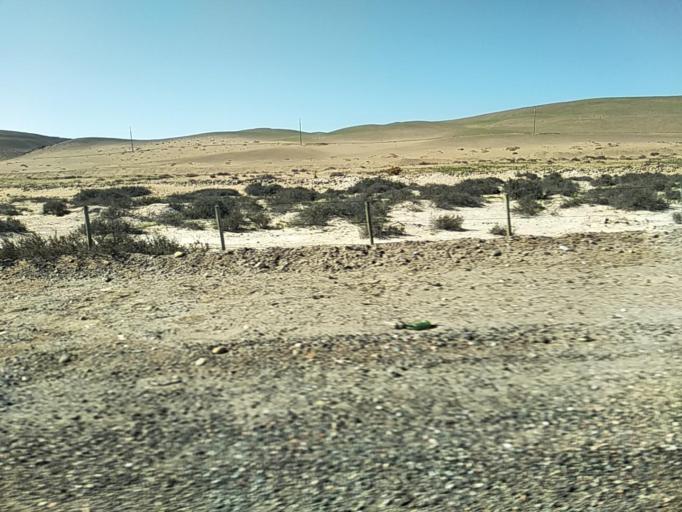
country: CL
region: Atacama
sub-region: Provincia de Copiapo
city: Copiapo
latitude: -27.3453
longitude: -70.7452
